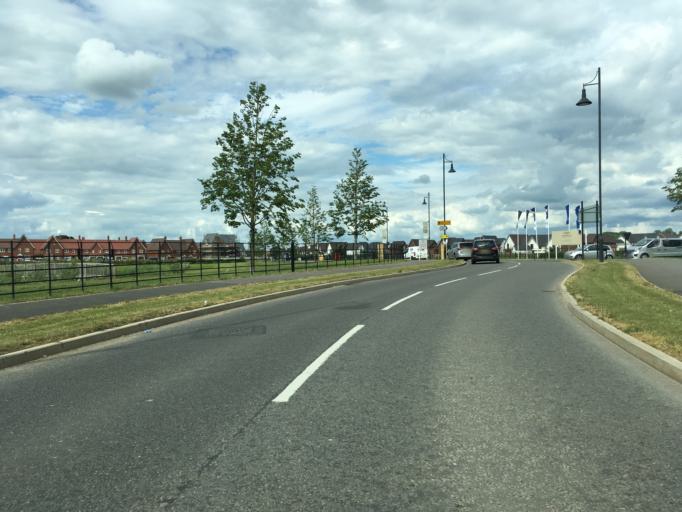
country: GB
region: England
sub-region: Wiltshire
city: Purton
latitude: 51.6058
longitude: -1.8285
